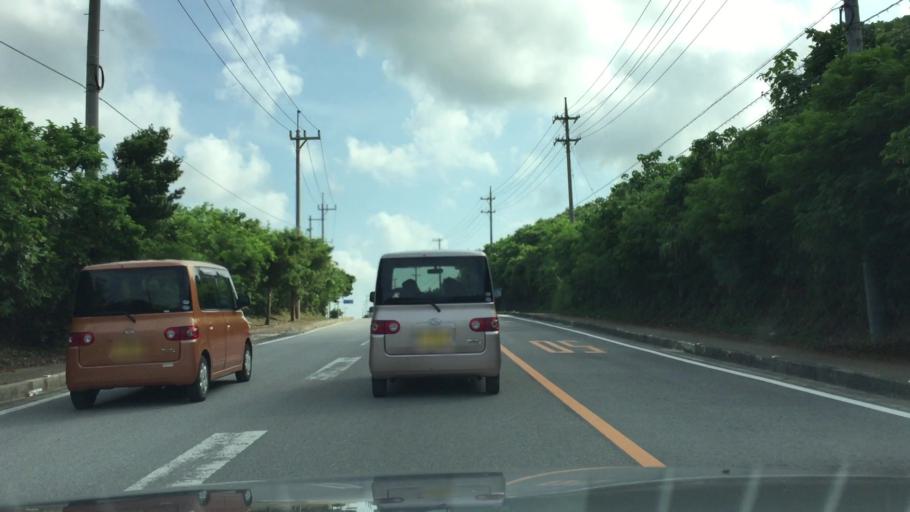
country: JP
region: Okinawa
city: Ishigaki
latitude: 24.4288
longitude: 124.2468
